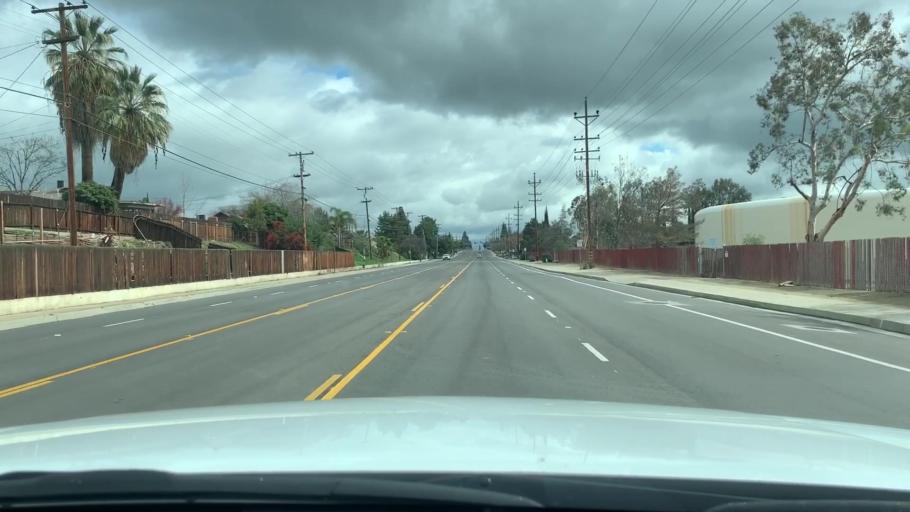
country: US
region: California
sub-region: Kern County
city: Bakersfield
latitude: 35.3977
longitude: -118.9479
